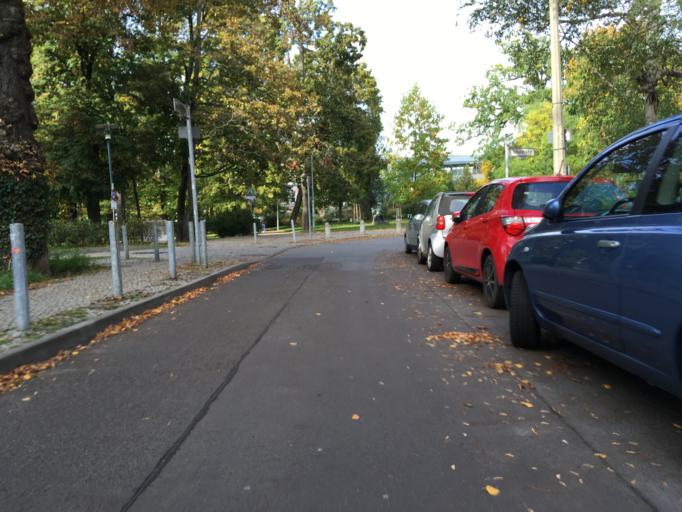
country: DE
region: Berlin
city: Pankow
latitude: 52.5684
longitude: 13.4070
